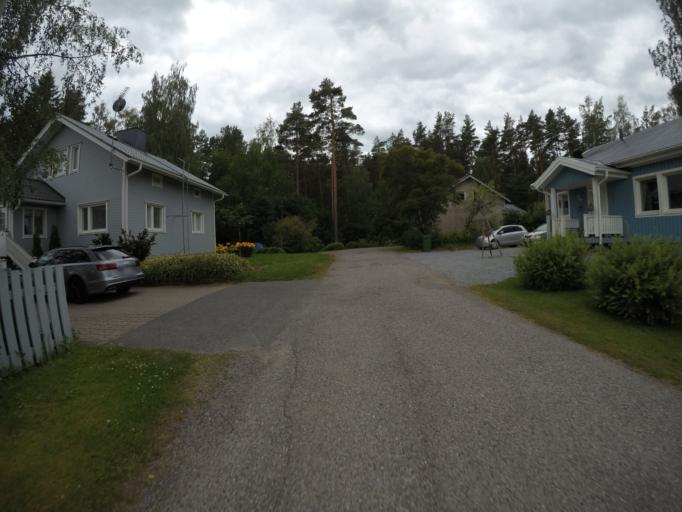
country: FI
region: Haeme
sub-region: Haemeenlinna
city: Haemeenlinna
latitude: 60.9802
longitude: 24.4493
